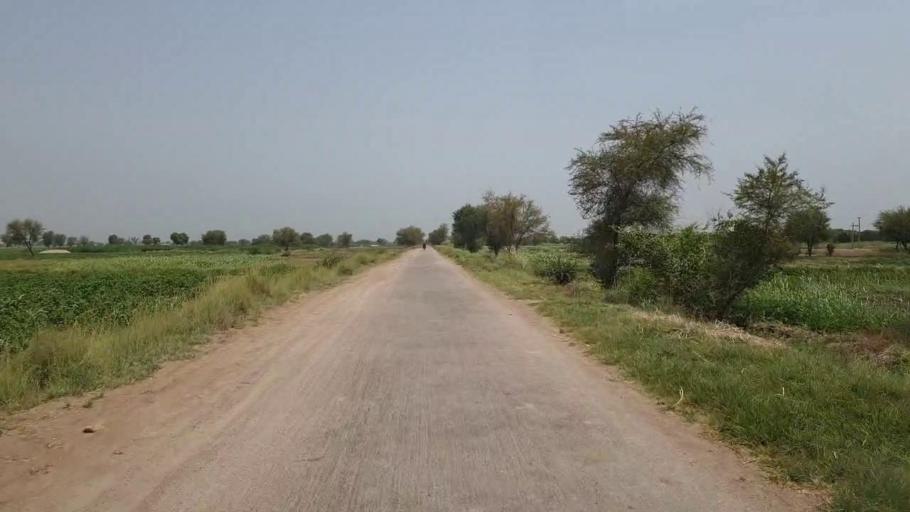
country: PK
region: Sindh
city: Nawabshah
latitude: 26.2608
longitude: 68.3190
